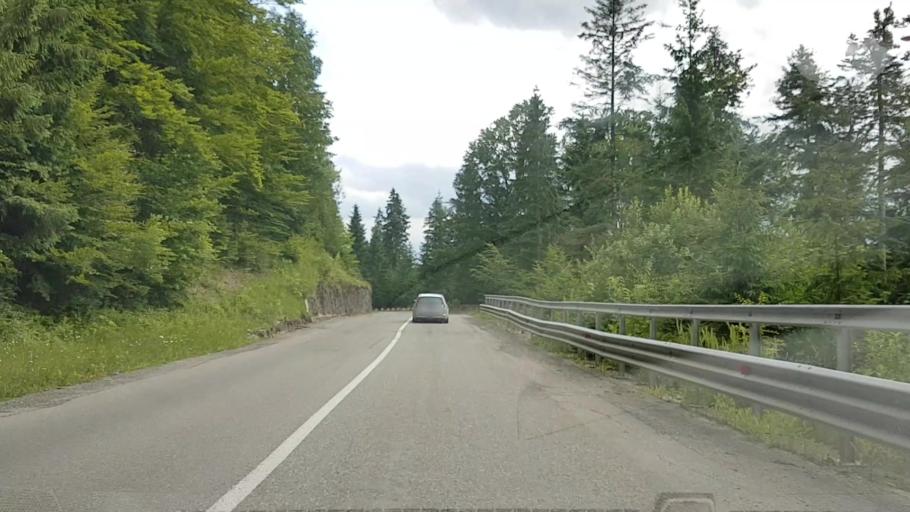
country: RO
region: Neamt
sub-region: Comuna Pangarati
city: Pangarati
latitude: 46.9746
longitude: 26.1168
